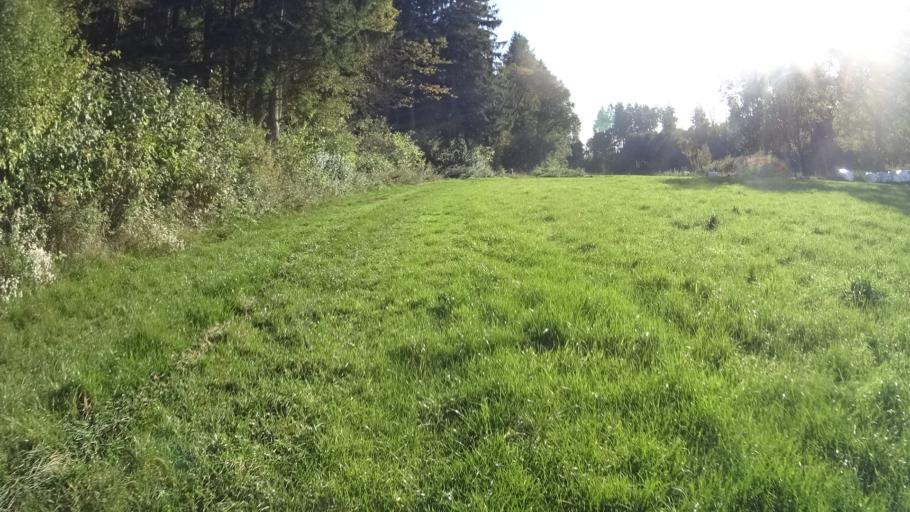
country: DE
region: Bavaria
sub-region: Upper Bavaria
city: Bohmfeld
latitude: 48.8496
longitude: 11.3637
